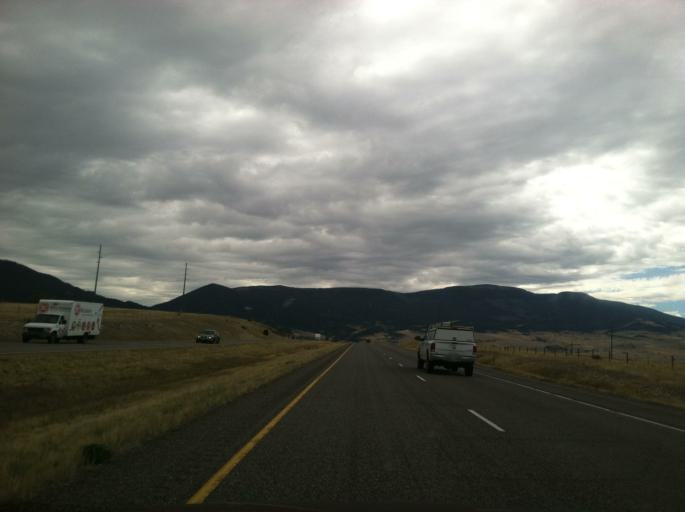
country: US
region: Montana
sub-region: Park County
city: Livingston
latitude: 45.6513
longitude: -110.5435
